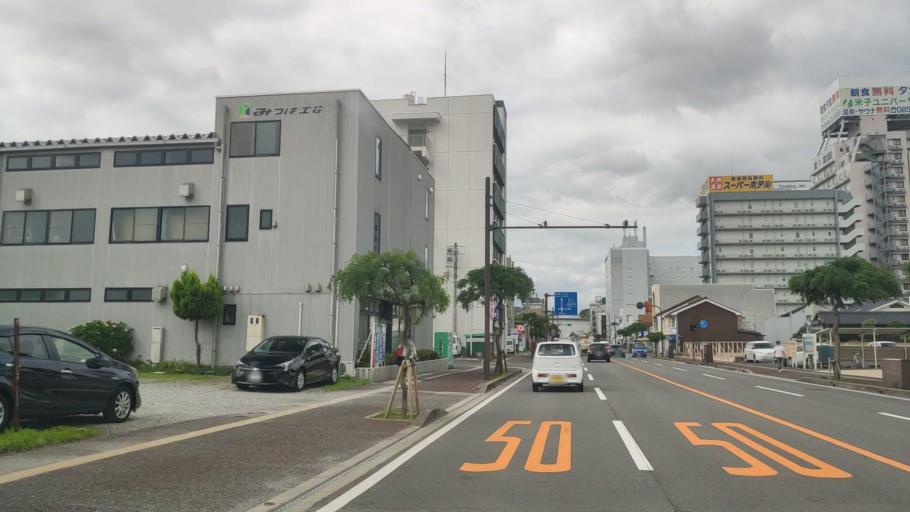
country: JP
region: Tottori
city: Yonago
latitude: 35.4259
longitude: 133.3375
